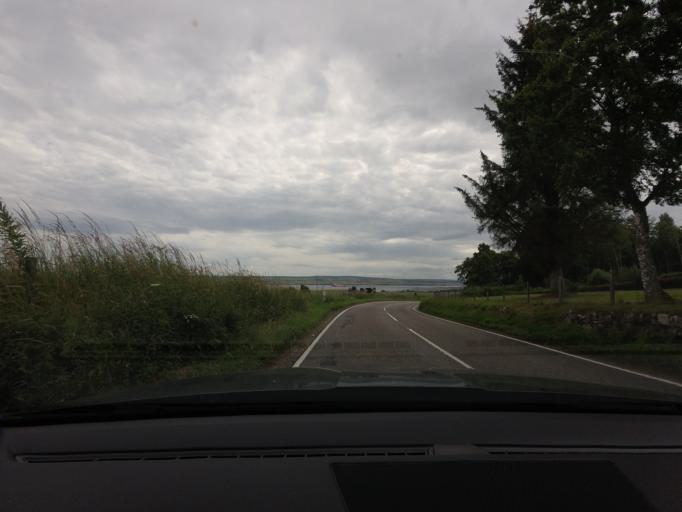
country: GB
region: Scotland
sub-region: Highland
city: Alness
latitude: 57.6978
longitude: -4.2881
